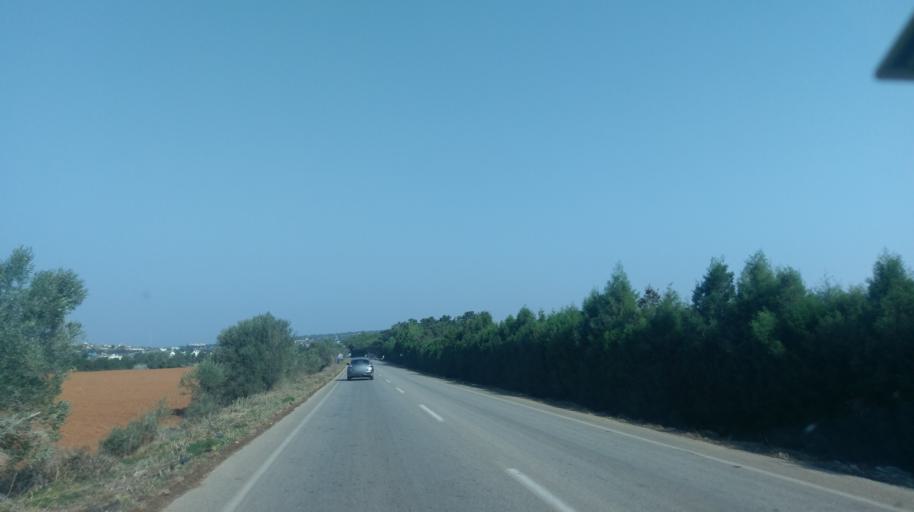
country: CY
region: Ammochostos
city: Leonarisso
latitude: 35.4910
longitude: 34.1545
